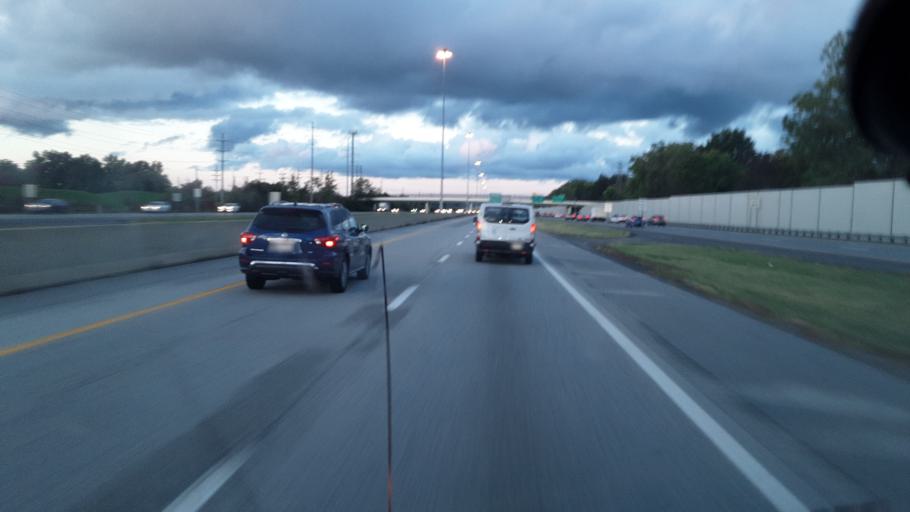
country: US
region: Ohio
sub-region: Cuyahoga County
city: Mayfield Heights
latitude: 41.5107
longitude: -81.4597
